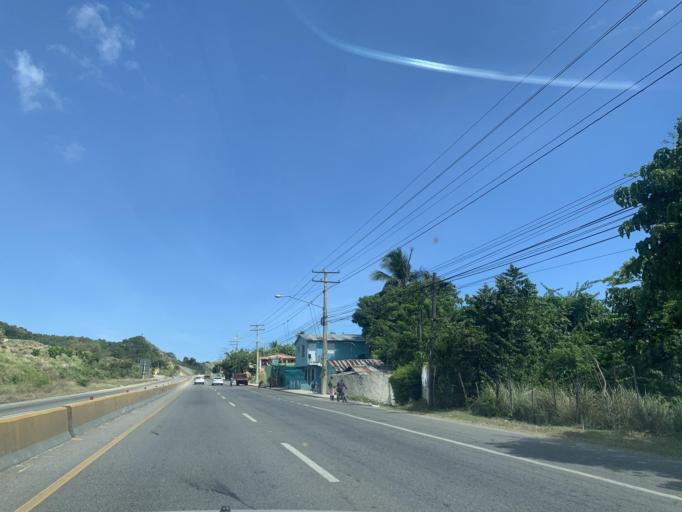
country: DO
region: Puerto Plata
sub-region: Puerto Plata
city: Puerto Plata
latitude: 19.8227
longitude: -70.7423
